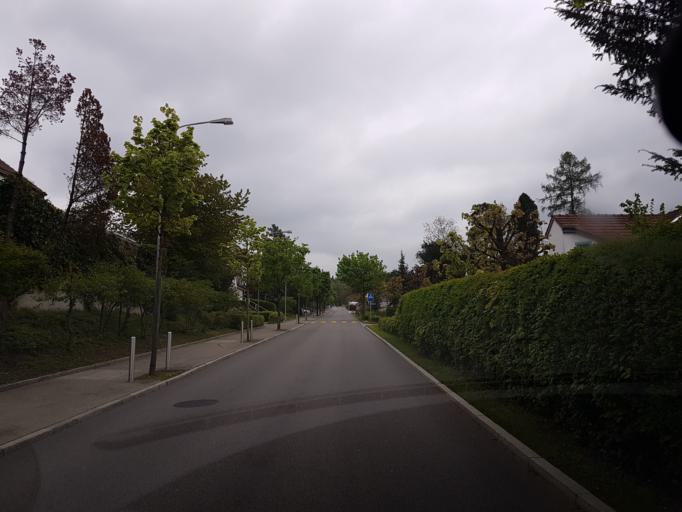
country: CH
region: Zurich
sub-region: Bezirk Dietikon
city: Uitikon
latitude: 47.3698
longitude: 8.4567
